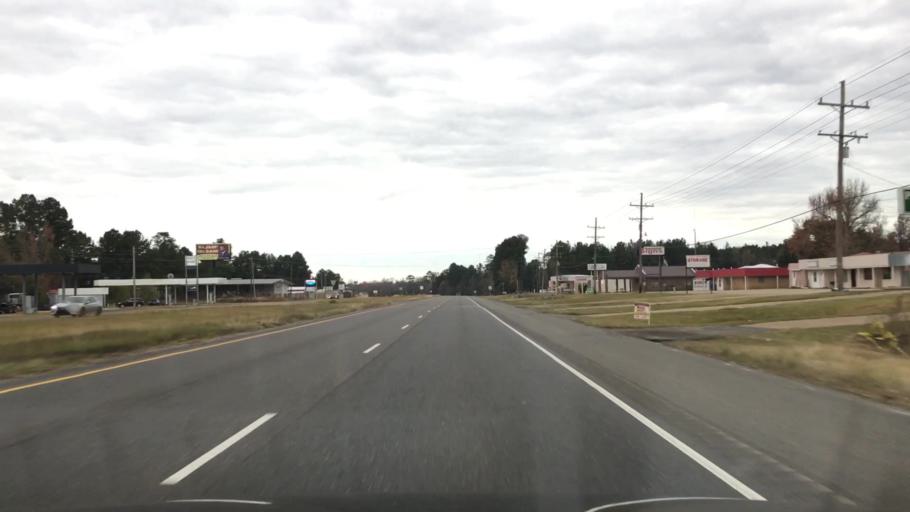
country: US
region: Louisiana
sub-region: Vernon Parish
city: New Llano
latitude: 31.0751
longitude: -93.2735
